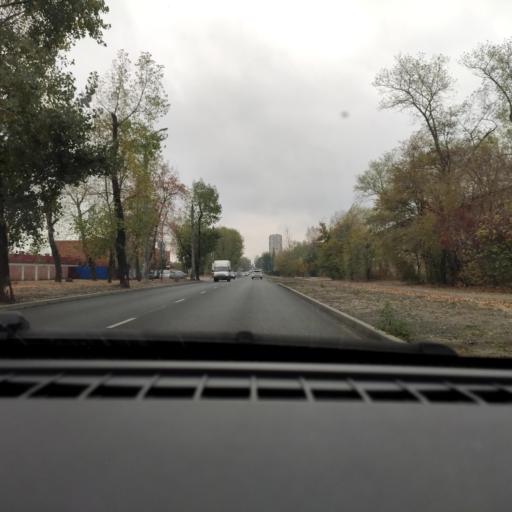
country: RU
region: Voronezj
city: Voronezh
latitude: 51.6605
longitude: 39.2503
